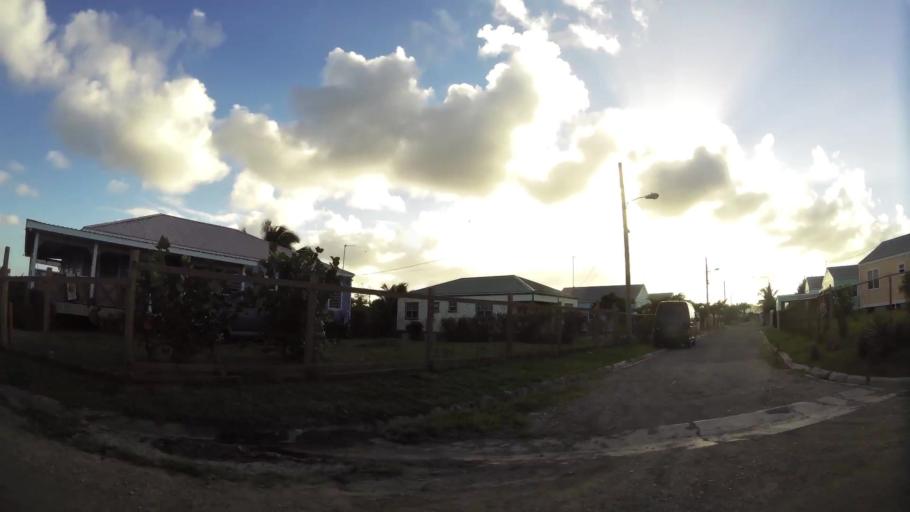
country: AG
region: Saint George
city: Piggotts
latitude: 17.1138
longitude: -61.7917
